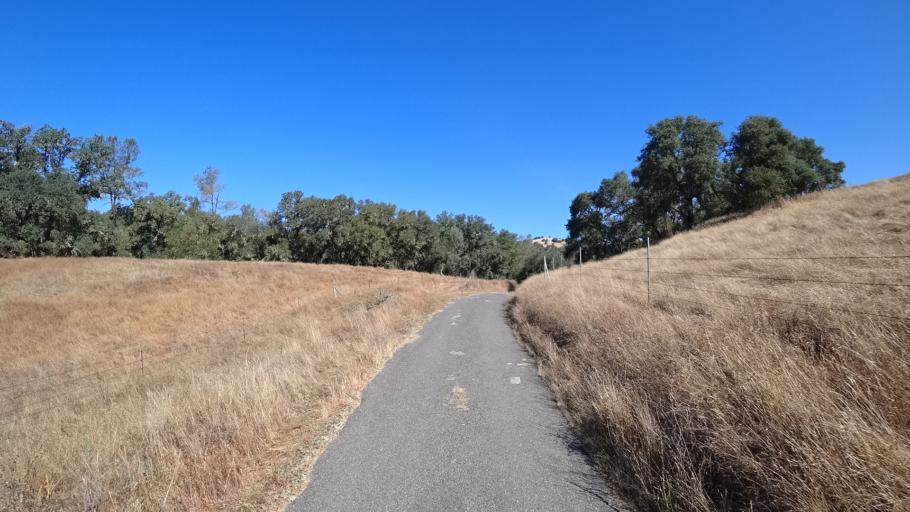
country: US
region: California
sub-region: Amador County
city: Jackson
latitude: 38.2914
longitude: -120.7511
